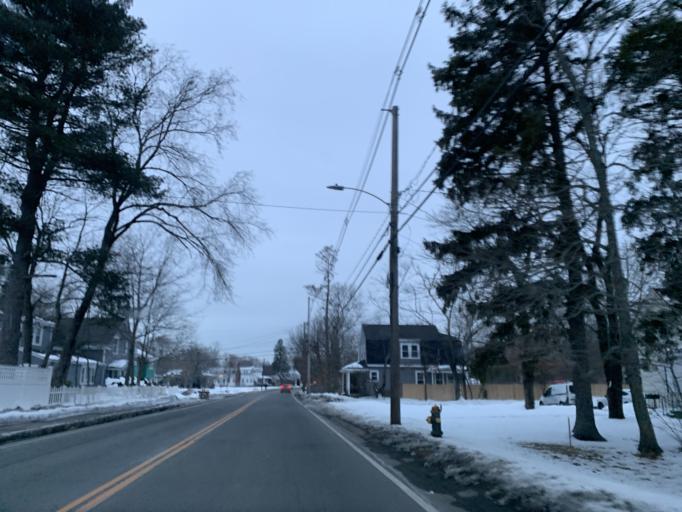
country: US
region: Massachusetts
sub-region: Norfolk County
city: Stoughton
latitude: 42.1374
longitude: -71.1131
